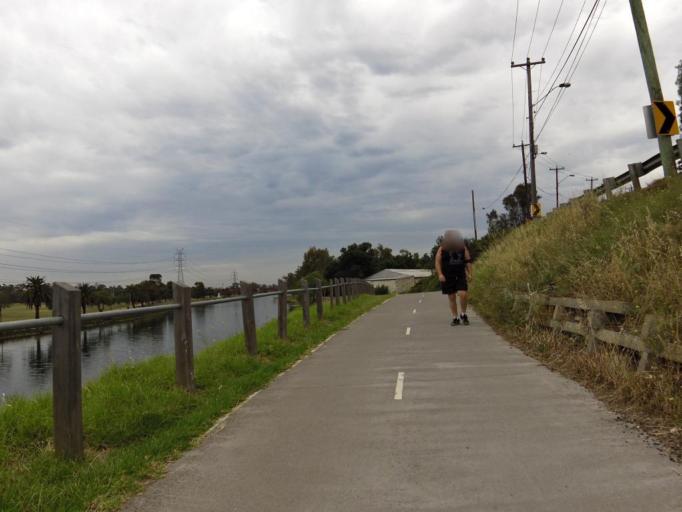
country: AU
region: Victoria
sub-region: Maribyrnong
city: Maribyrnong
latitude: -37.7739
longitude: 144.8956
